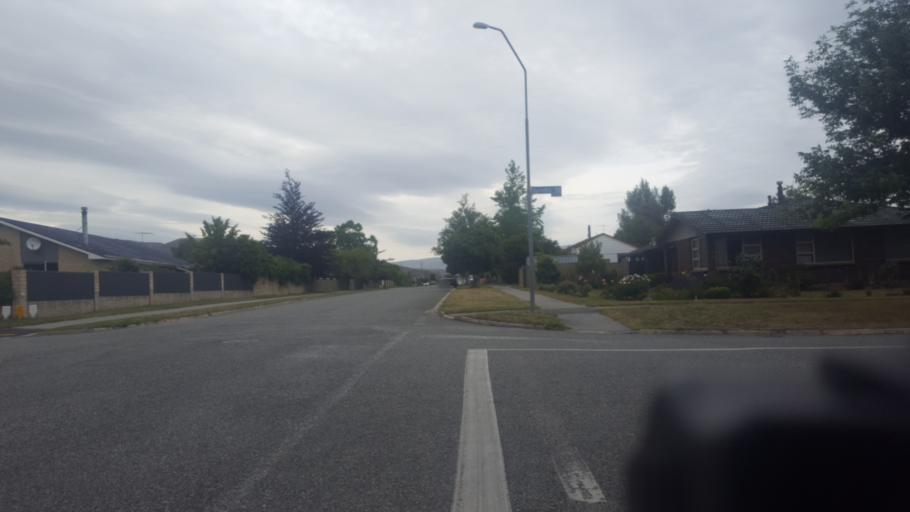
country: NZ
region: Otago
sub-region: Queenstown-Lakes District
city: Wanaka
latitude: -45.0416
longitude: 169.2058
